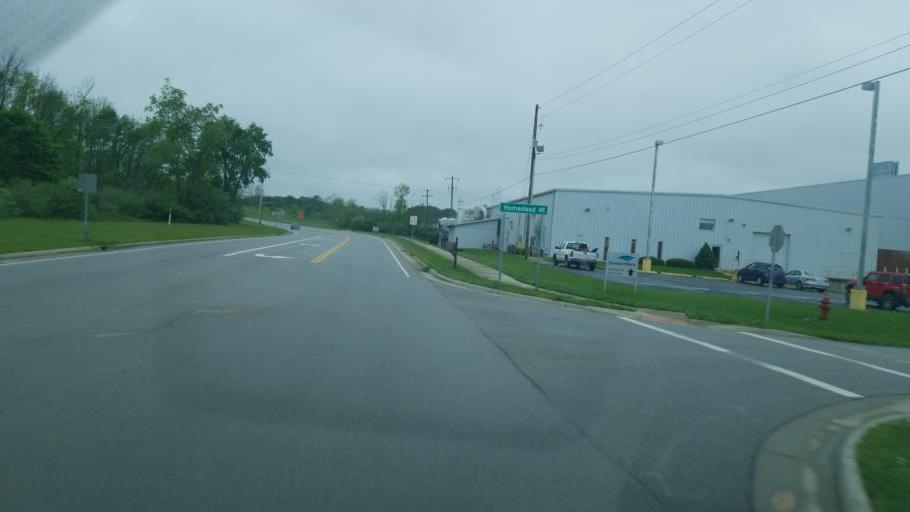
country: US
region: Ohio
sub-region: Highland County
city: Hillsboro
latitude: 39.2341
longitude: -83.6171
